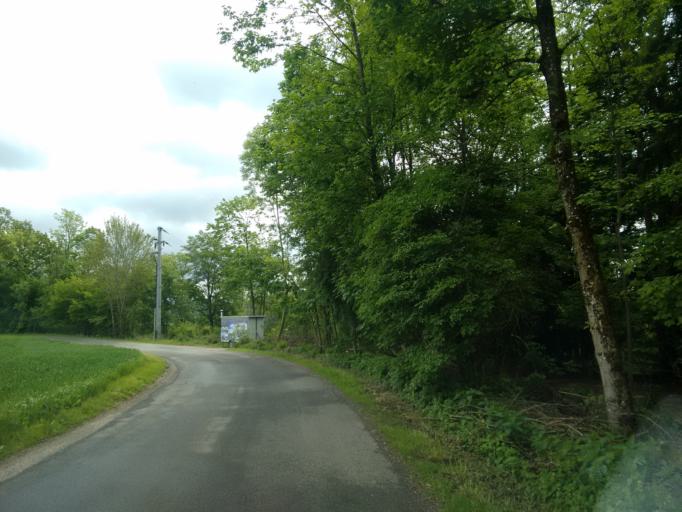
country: AT
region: Upper Austria
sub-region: Politischer Bezirk Steyr-Land
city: Sierning
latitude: 48.0182
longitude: 14.3107
